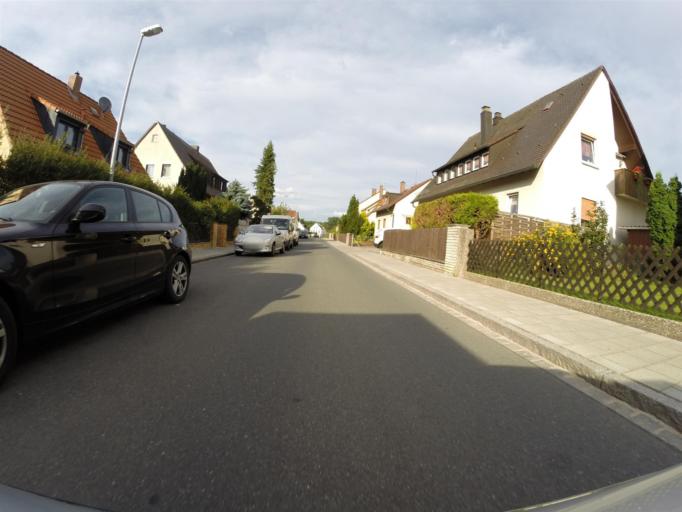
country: DE
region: Bavaria
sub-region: Regierungsbezirk Mittelfranken
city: Stein
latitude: 49.4012
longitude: 11.0091
